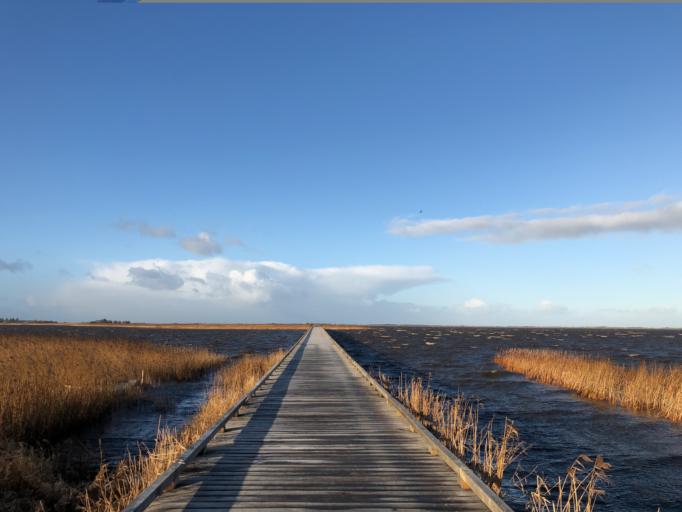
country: DK
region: Central Jutland
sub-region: Ringkobing-Skjern Kommune
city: Ringkobing
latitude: 56.1509
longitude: 8.2397
